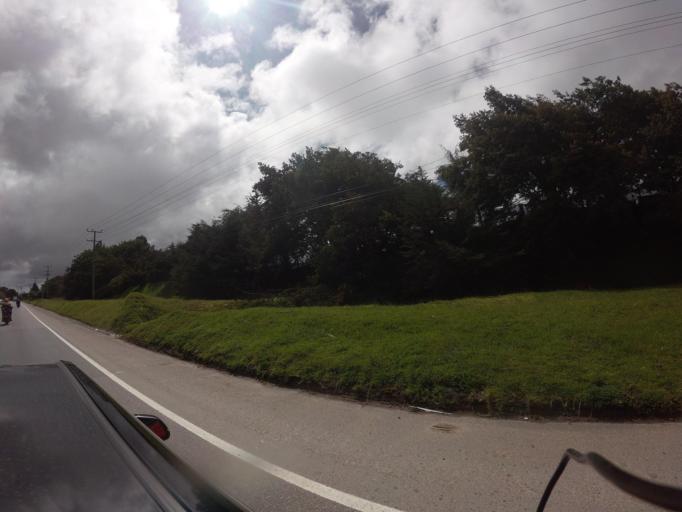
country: CO
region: Cundinamarca
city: Choconta
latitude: 5.0994
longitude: -73.7119
